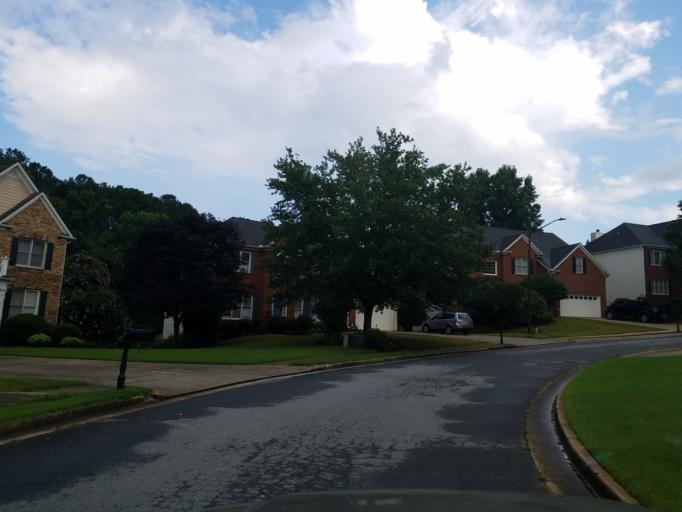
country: US
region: Georgia
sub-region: Cherokee County
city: Woodstock
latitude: 34.0558
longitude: -84.4875
